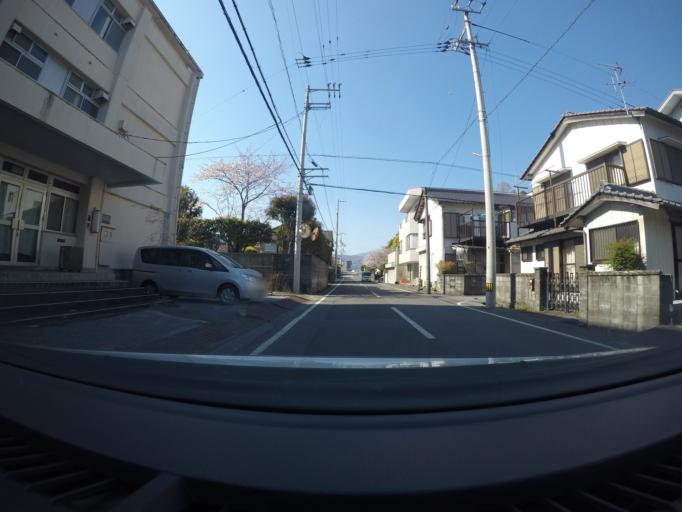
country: JP
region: Kochi
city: Kochi-shi
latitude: 33.5478
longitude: 133.5690
